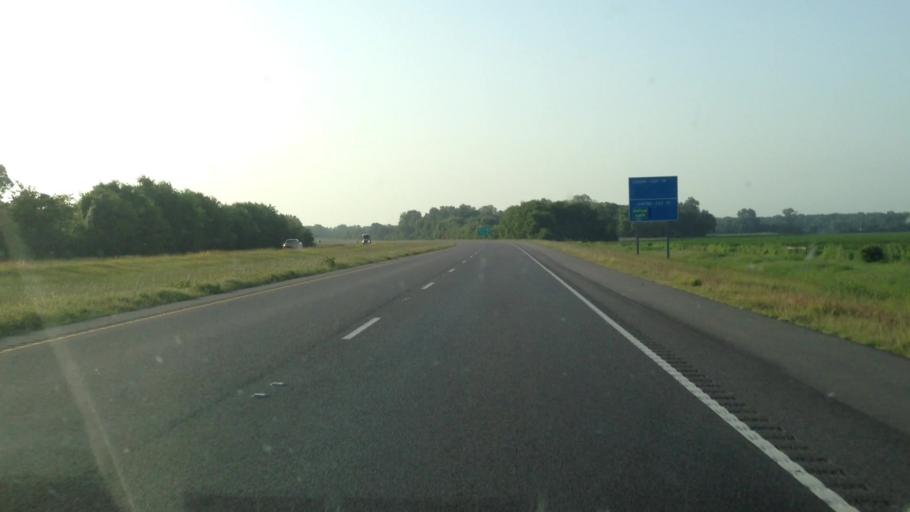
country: US
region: Louisiana
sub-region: Rapides Parish
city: Boyce
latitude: 31.3837
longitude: -92.6807
